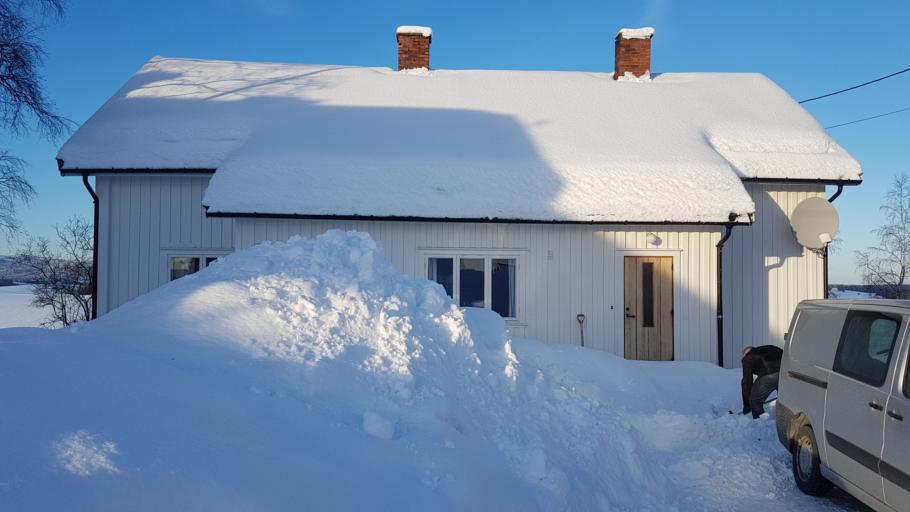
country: NO
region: Akershus
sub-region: Nannestad
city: Teigebyen
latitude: 60.1700
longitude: 11.0194
